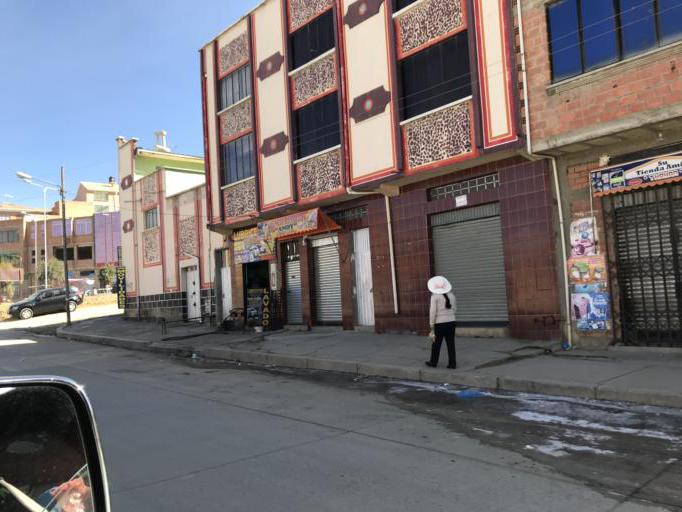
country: BO
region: La Paz
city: La Paz
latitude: -16.4858
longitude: -68.2057
